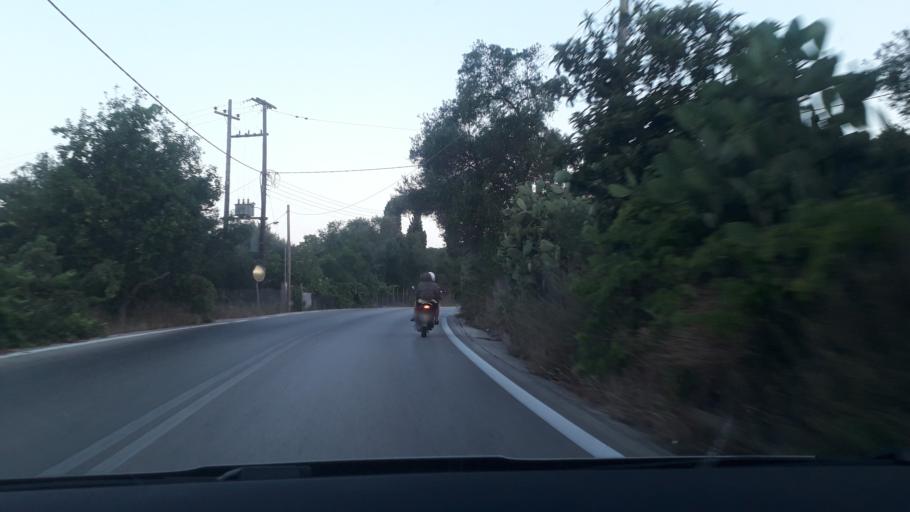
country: GR
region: Ionian Islands
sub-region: Nomos Kerkyras
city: Agios Matthaios
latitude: 39.4536
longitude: 19.9234
